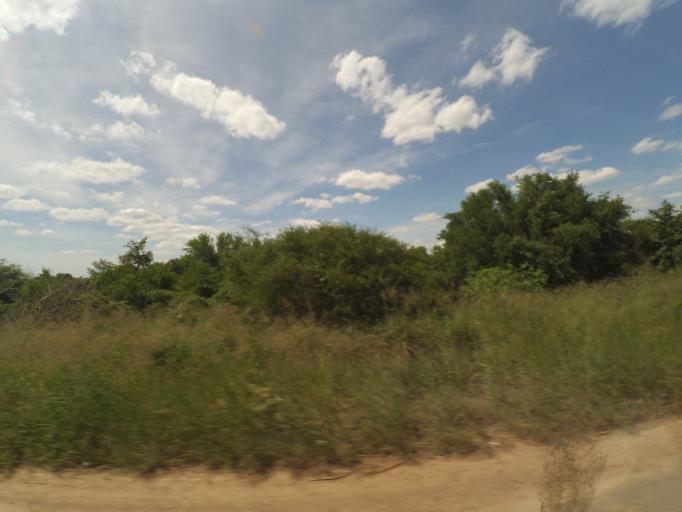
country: BO
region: Santa Cruz
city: Pailon
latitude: -17.5907
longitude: -61.9809
